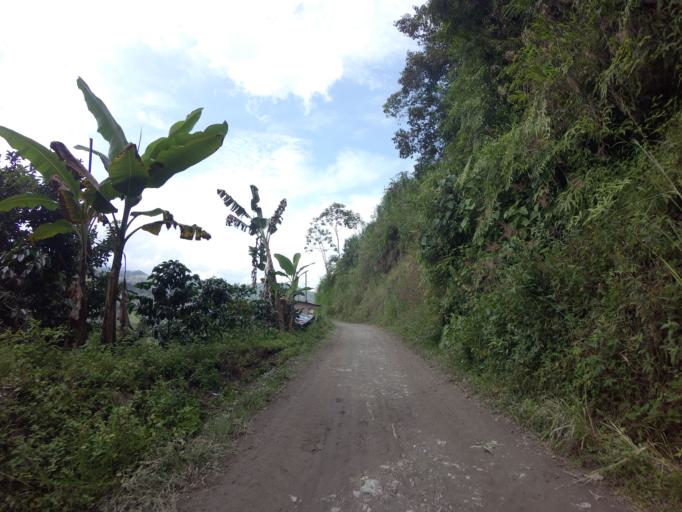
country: CO
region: Caldas
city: Marquetalia
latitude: 5.3158
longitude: -75.0480
